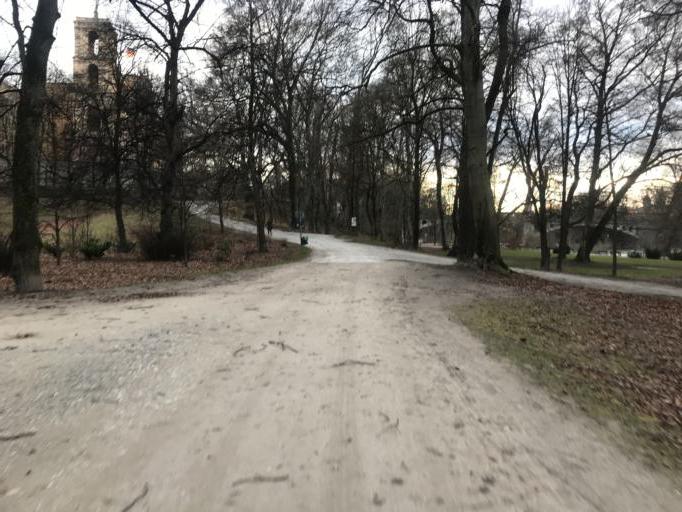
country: DE
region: Bavaria
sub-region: Upper Bavaria
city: Munich
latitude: 48.1383
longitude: 11.5944
